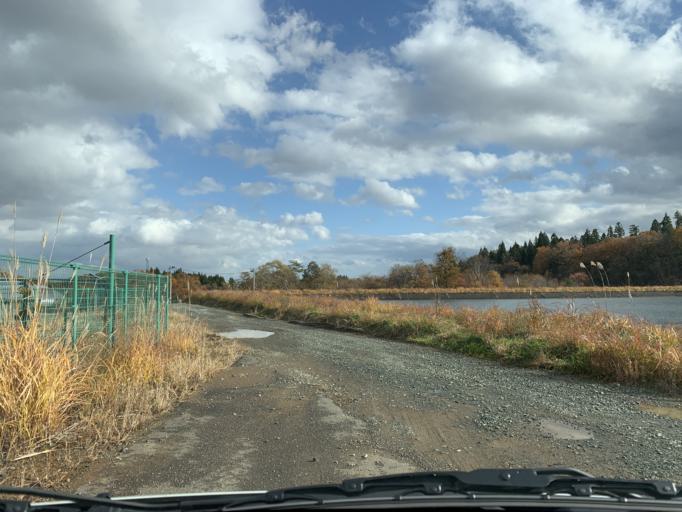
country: JP
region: Iwate
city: Mizusawa
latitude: 39.1125
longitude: 140.9562
